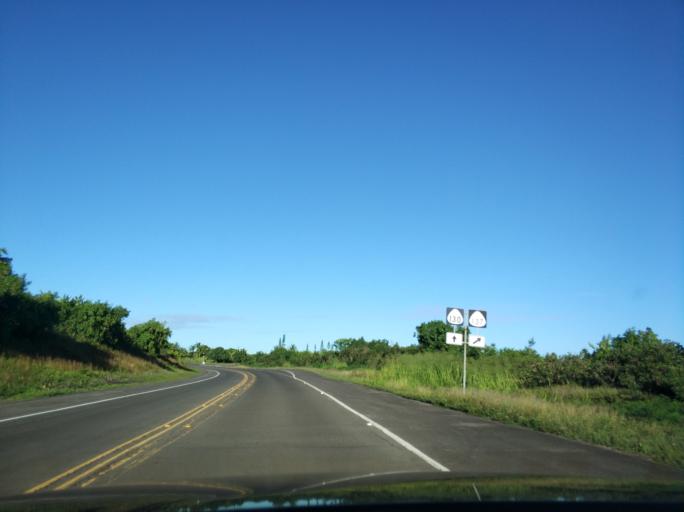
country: US
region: Hawaii
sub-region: Hawaii County
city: Leilani Estates
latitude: 19.3664
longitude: -154.9679
